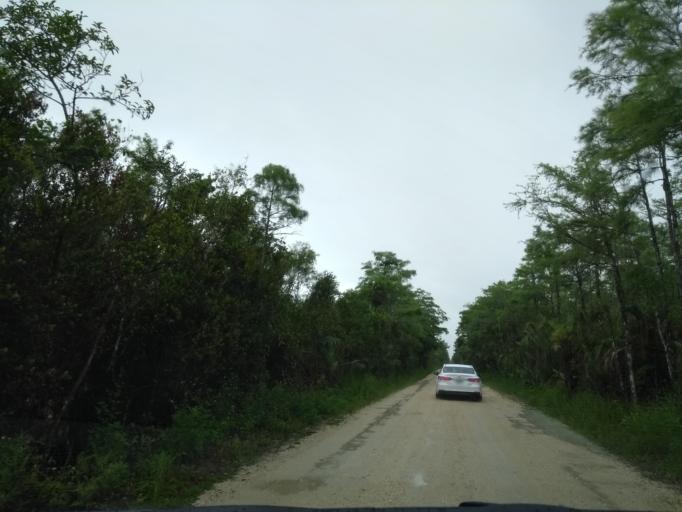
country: US
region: Florida
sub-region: Miami-Dade County
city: The Hammocks
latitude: 25.7602
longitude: -81.0359
